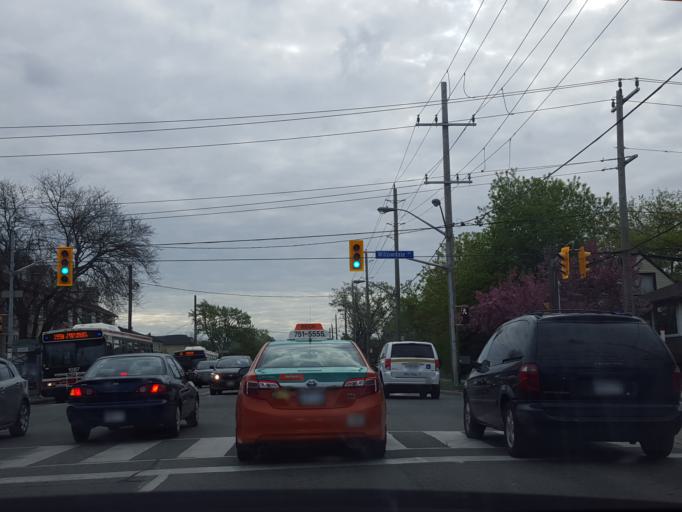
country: CA
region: Ontario
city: Willowdale
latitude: 43.7815
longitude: -79.4074
